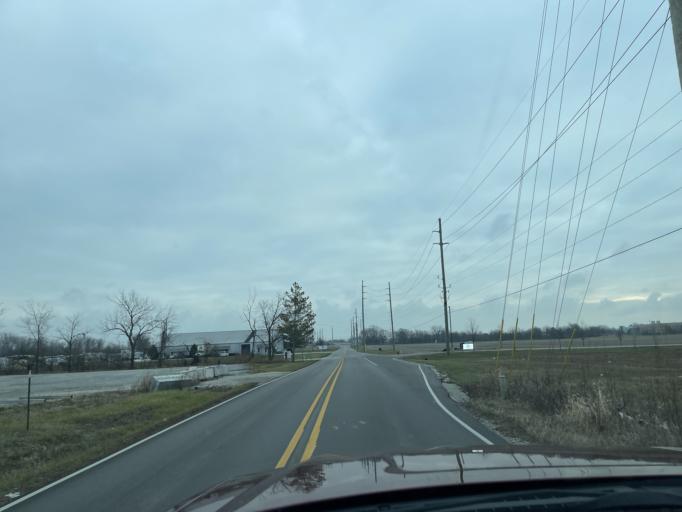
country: US
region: Indiana
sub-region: Boone County
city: Whitestown
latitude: 39.9459
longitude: -86.3659
